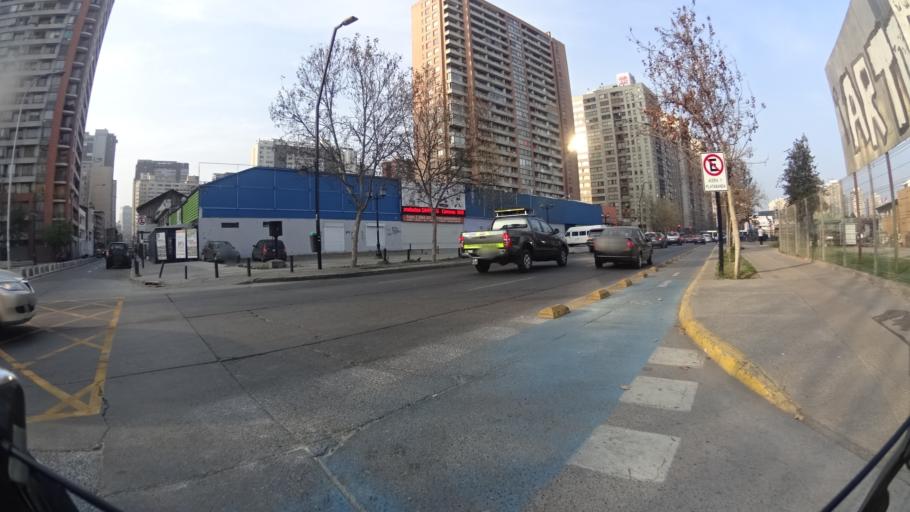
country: CL
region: Santiago Metropolitan
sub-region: Provincia de Santiago
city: Santiago
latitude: -33.4511
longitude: -70.6483
